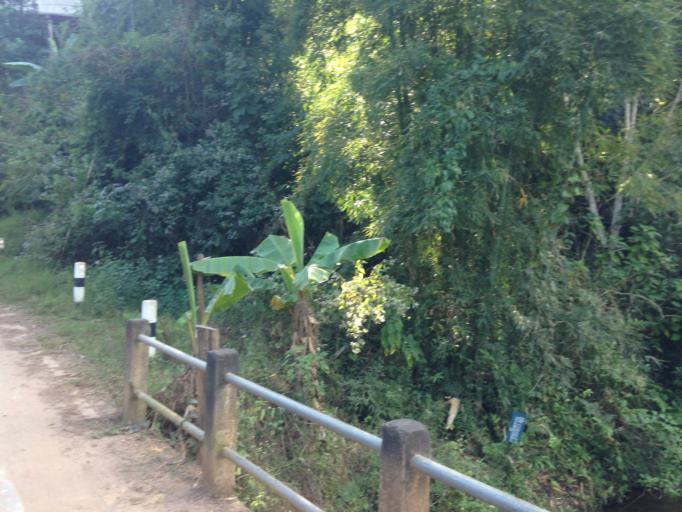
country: TH
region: Chiang Mai
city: Chaem Luang
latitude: 18.9999
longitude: 98.2710
